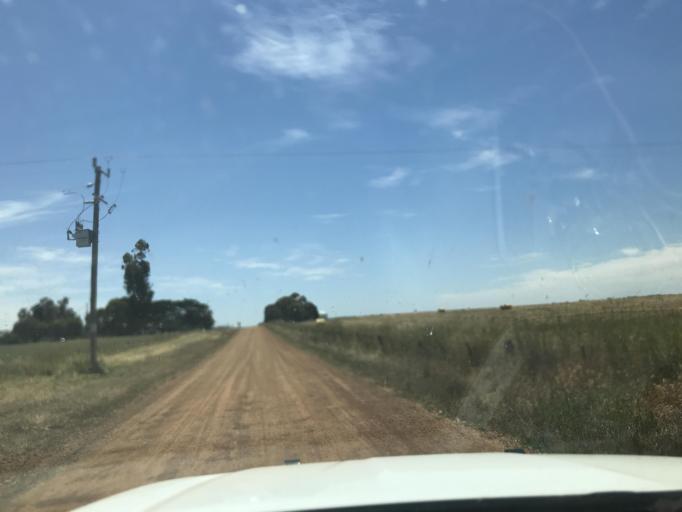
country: AU
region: Victoria
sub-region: Horsham
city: Horsham
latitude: -36.9789
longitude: 141.5311
